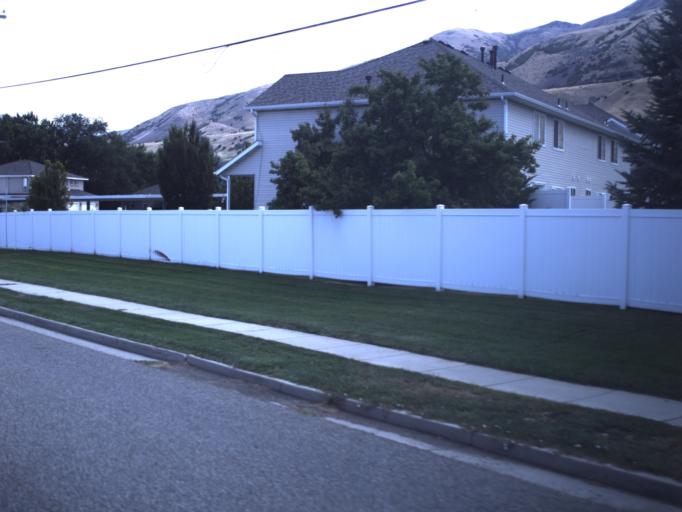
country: US
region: Utah
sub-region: Box Elder County
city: Perry
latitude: 41.4673
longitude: -112.0315
